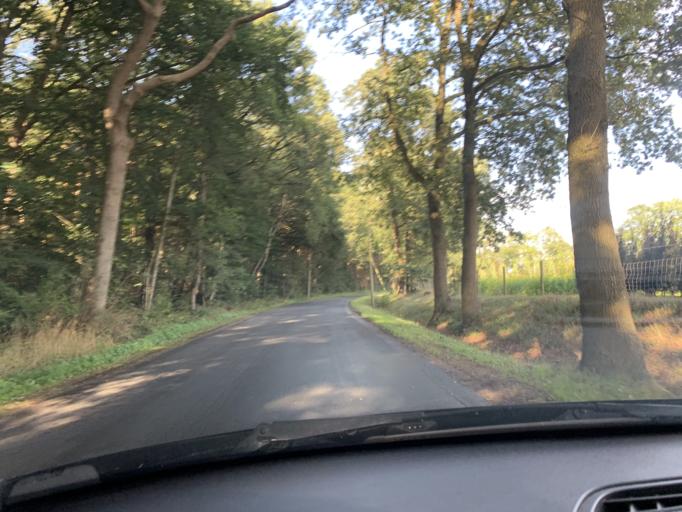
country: DE
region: Lower Saxony
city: Westerstede
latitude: 53.2012
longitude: 7.9154
